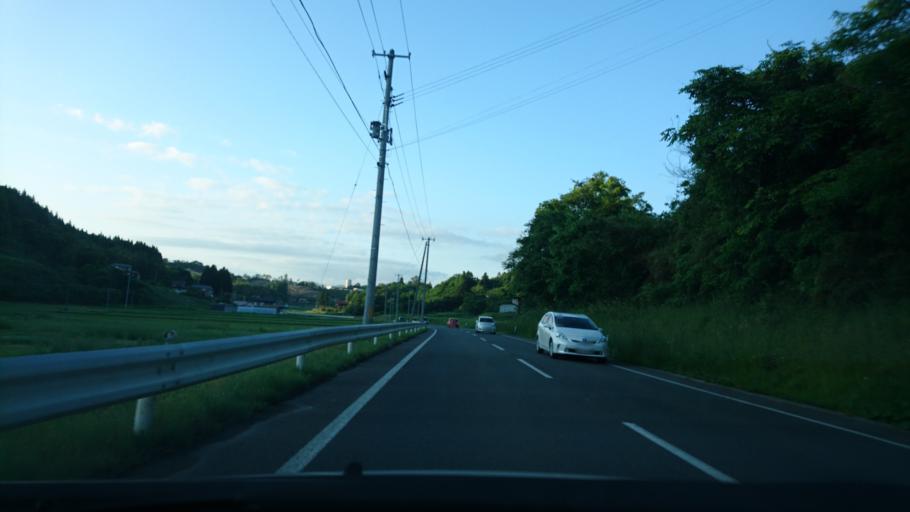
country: JP
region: Iwate
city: Ichinoseki
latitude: 38.8934
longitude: 141.1587
